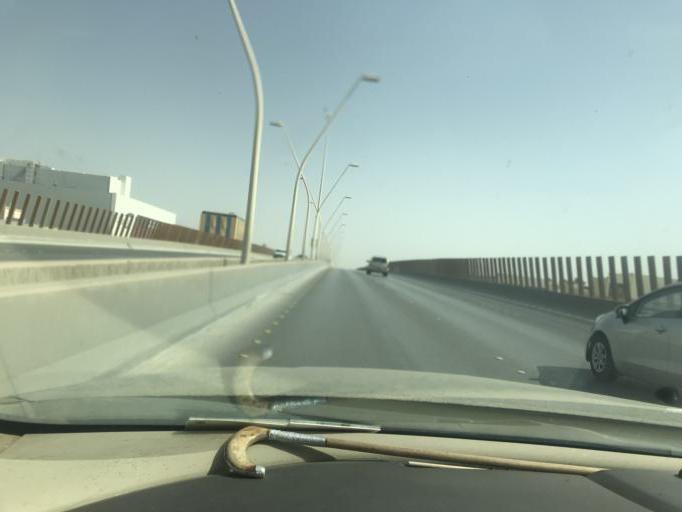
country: SA
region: Ar Riyad
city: Riyadh
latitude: 24.7464
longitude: 46.7020
